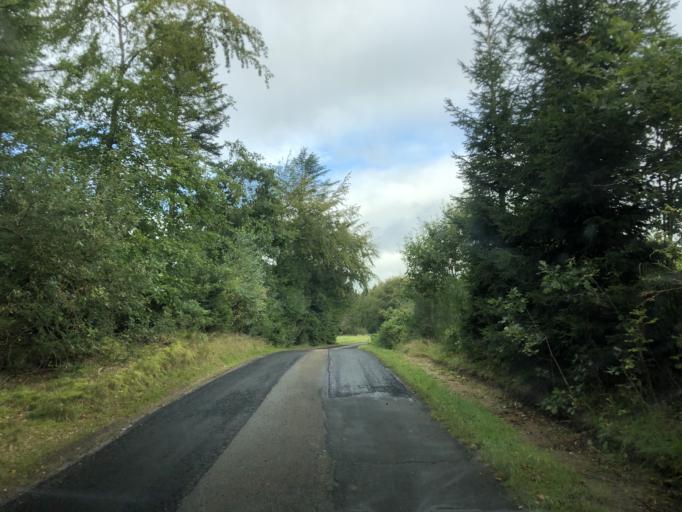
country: DK
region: Central Jutland
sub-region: Holstebro Kommune
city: Ulfborg
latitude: 56.3069
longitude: 8.4319
